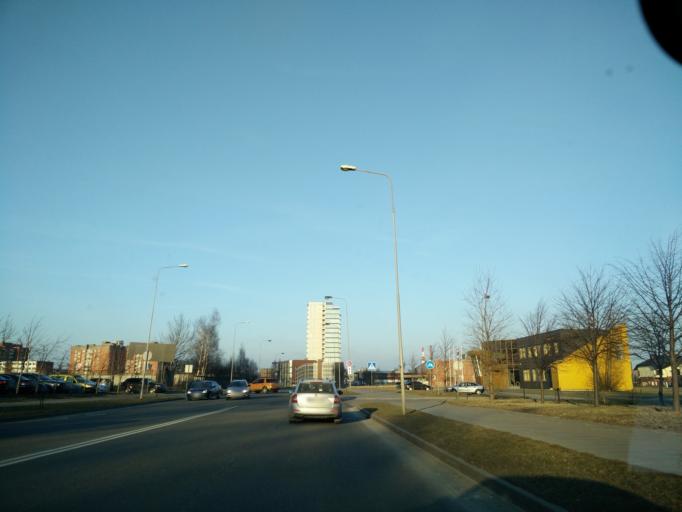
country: LT
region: Klaipedos apskritis
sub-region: Klaipeda
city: Klaipeda
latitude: 55.6904
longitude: 21.1466
